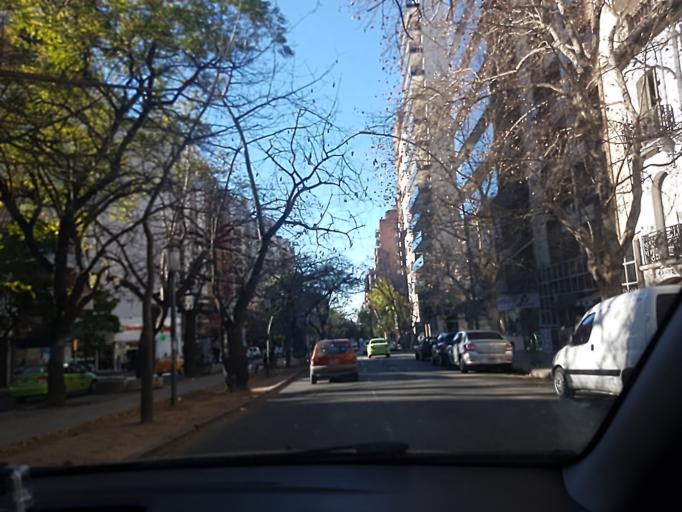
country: AR
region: Cordoba
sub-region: Departamento de Capital
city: Cordoba
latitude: -31.4249
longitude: -64.1832
